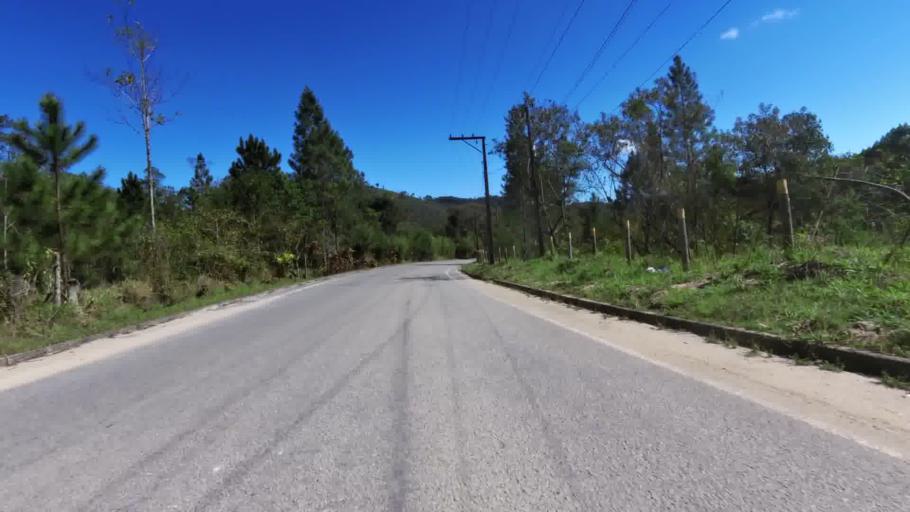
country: BR
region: Espirito Santo
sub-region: Vargem Alta
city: Vargem Alta
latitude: -20.6788
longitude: -40.9524
